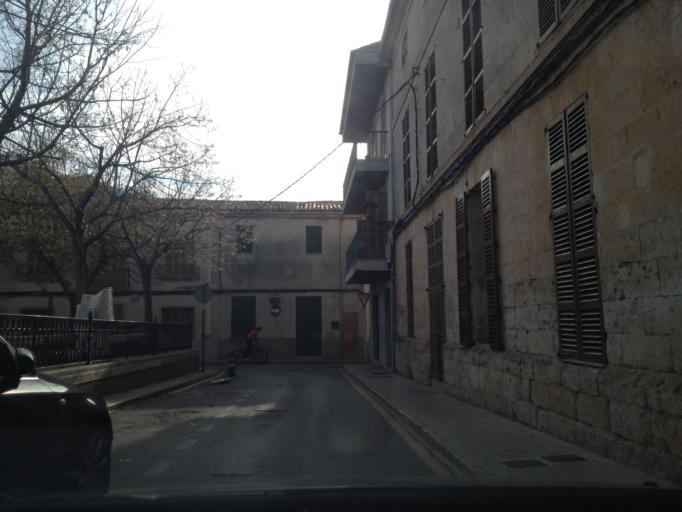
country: ES
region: Balearic Islands
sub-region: Illes Balears
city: Muro
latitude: 39.7368
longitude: 3.0569
